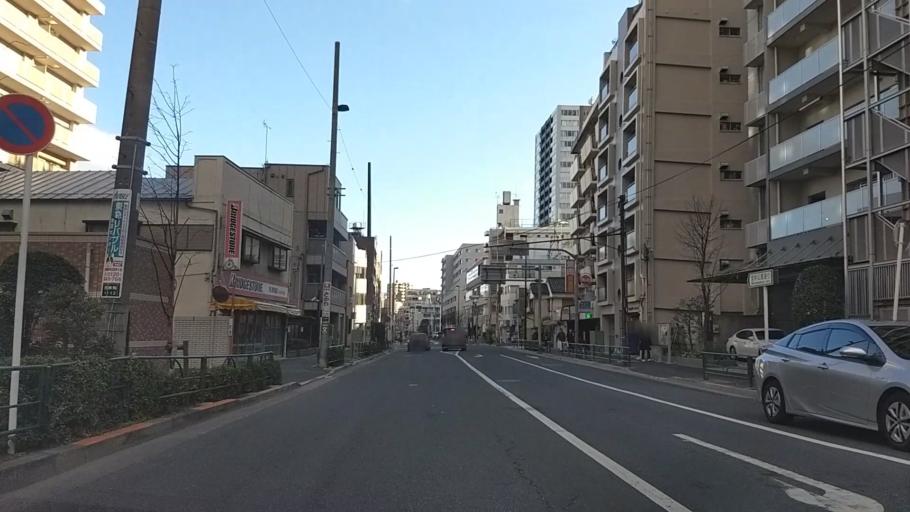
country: JP
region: Tokyo
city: Tokyo
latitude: 35.7384
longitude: 139.7225
